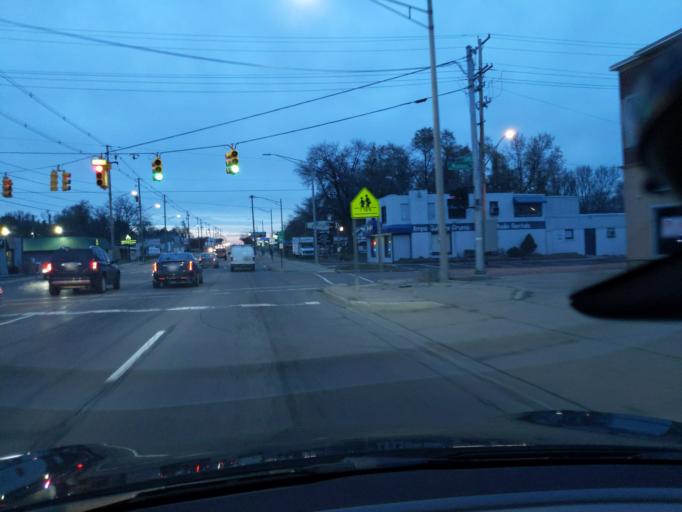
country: US
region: Michigan
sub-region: Ingham County
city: Lansing
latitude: 42.6971
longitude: -84.5480
